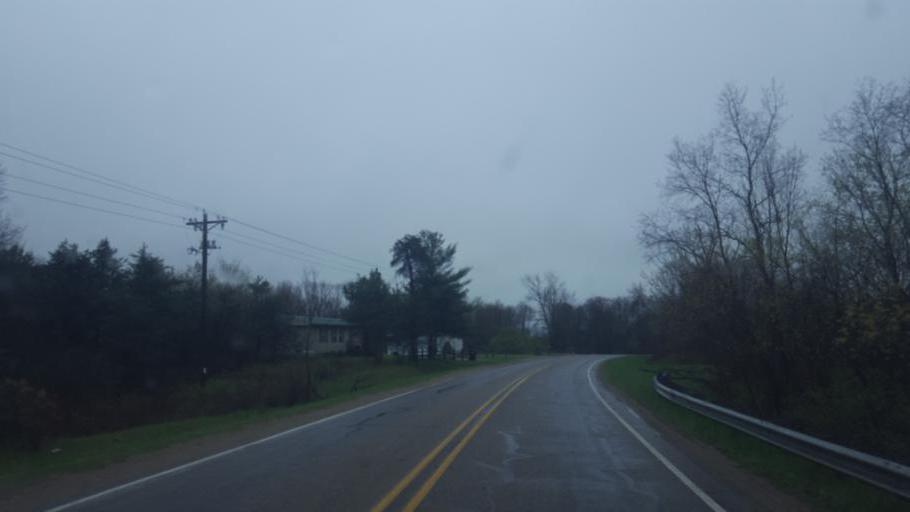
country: US
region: Michigan
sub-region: Isabella County
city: Lake Isabella
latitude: 43.5665
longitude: -84.9857
